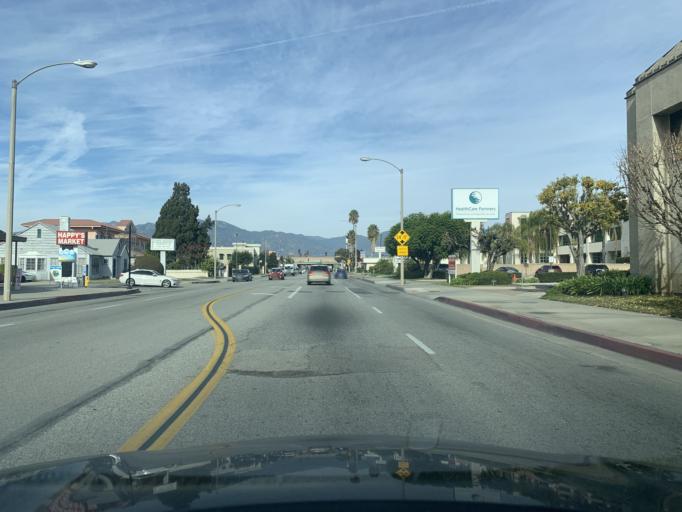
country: US
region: California
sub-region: Los Angeles County
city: South El Monte
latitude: 34.0655
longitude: -118.0427
